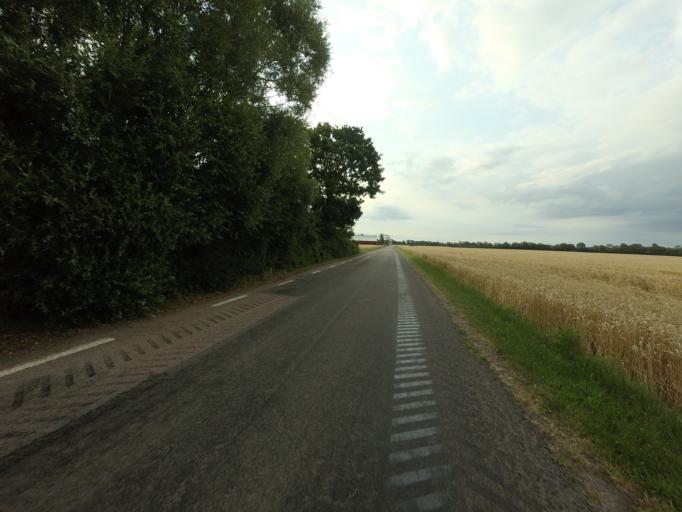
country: SE
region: Skane
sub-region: Hoganas Kommun
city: Hoganas
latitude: 56.1522
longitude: 12.6420
